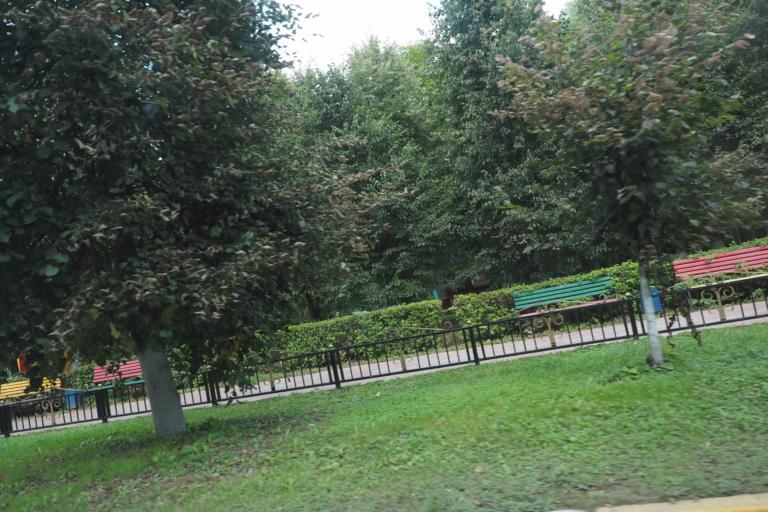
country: RU
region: Moskovskaya
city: Ramenskoye
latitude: 55.5897
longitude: 38.2090
